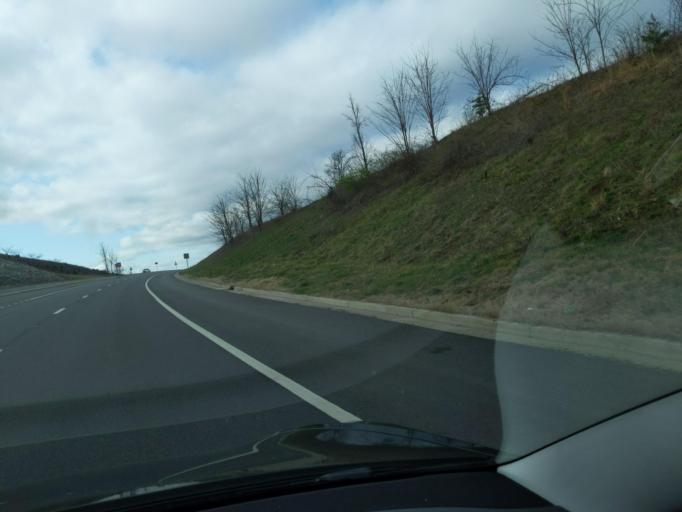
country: US
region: Tennessee
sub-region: Hamblen County
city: Morristown
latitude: 36.1694
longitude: -83.3427
